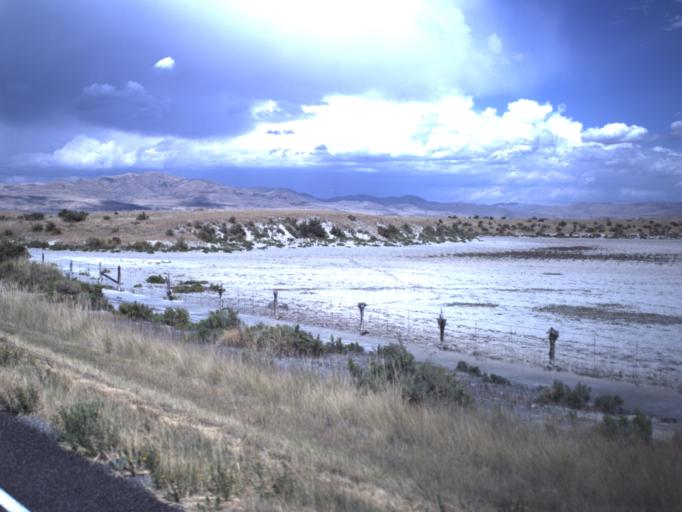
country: US
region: Utah
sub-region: Box Elder County
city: Tremonton
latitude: 41.5864
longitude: -112.2658
